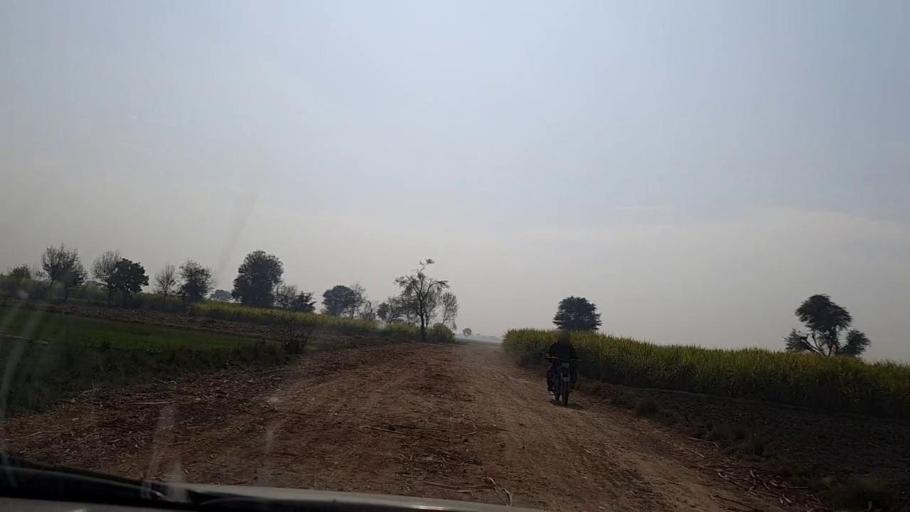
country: PK
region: Sindh
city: Daulatpur
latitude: 26.5407
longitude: 67.9878
